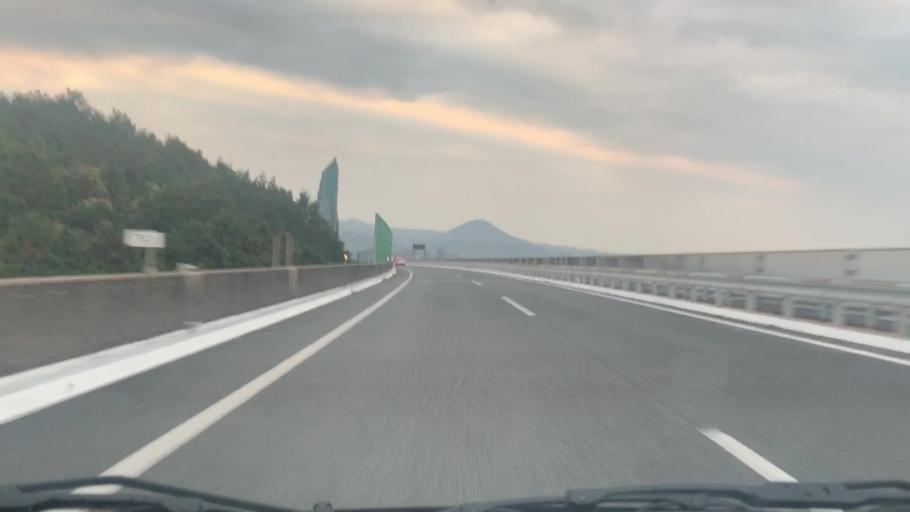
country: JP
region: Saga Prefecture
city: Ureshinomachi-shimojuku
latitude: 33.0300
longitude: 129.9302
